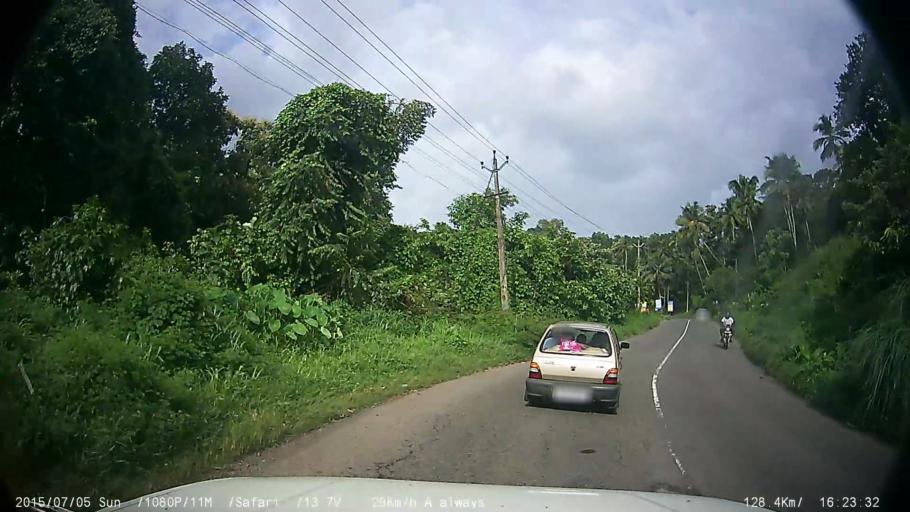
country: IN
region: Kerala
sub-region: Ernakulam
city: Muvattupuzha
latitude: 9.9632
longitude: 76.5776
